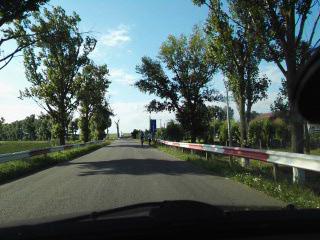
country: RO
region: Giurgiu
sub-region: Comuna Comana
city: Comana
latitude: 44.1886
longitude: 26.1341
